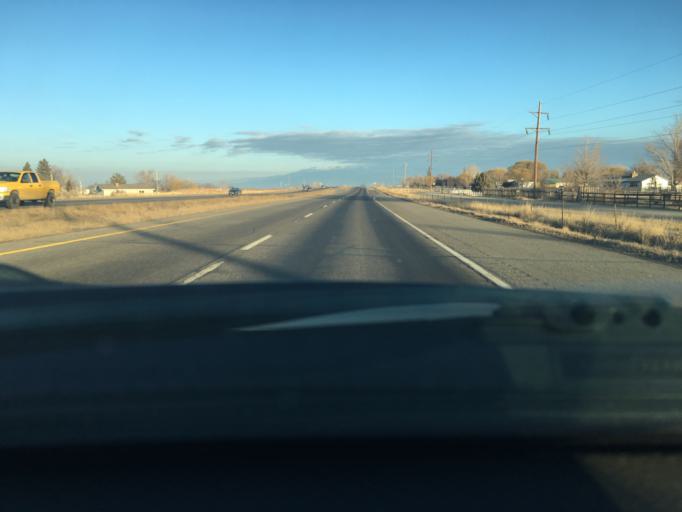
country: US
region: Colorado
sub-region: Montrose County
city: Olathe
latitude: 38.5551
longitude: -107.9512
